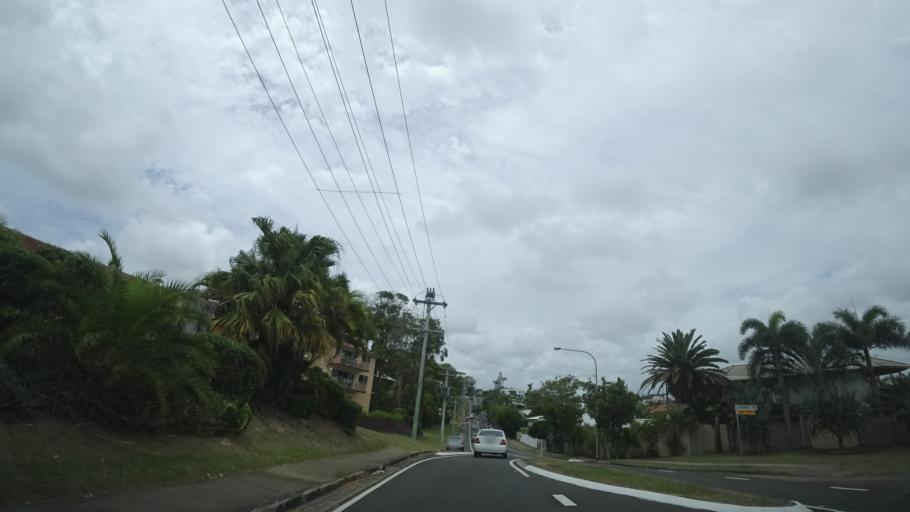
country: AU
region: Queensland
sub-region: Sunshine Coast
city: Mooloolaba
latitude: -26.6719
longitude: 153.1059
